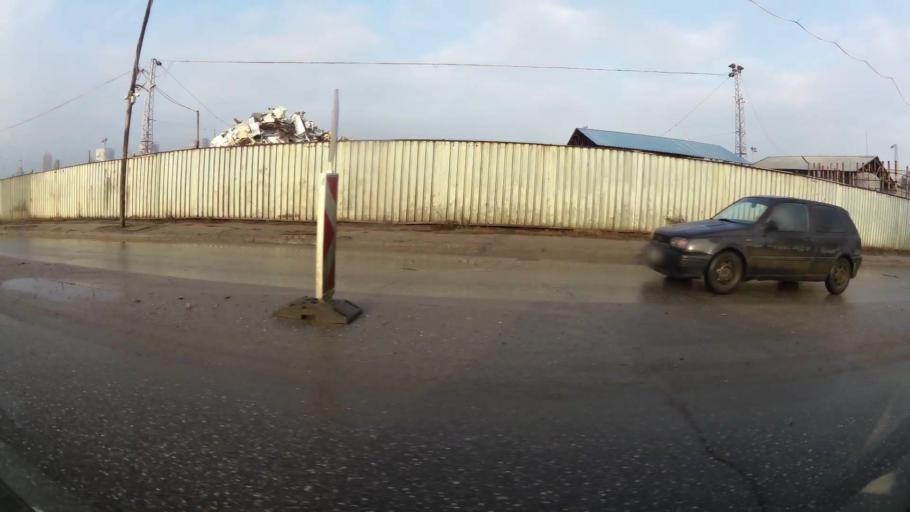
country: BG
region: Sofia-Capital
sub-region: Stolichna Obshtina
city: Sofia
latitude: 42.7282
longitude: 23.3186
